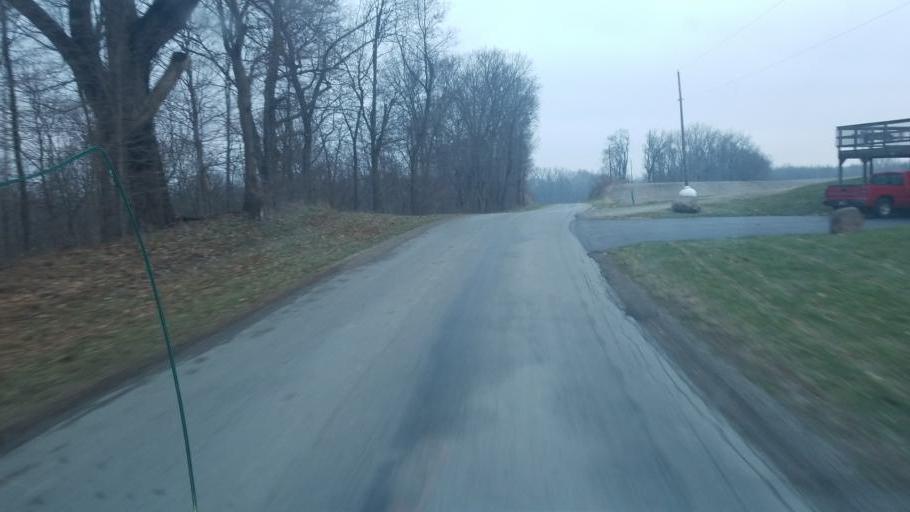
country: US
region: Ohio
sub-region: Seneca County
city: Tiffin
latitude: 40.9921
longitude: -83.2049
